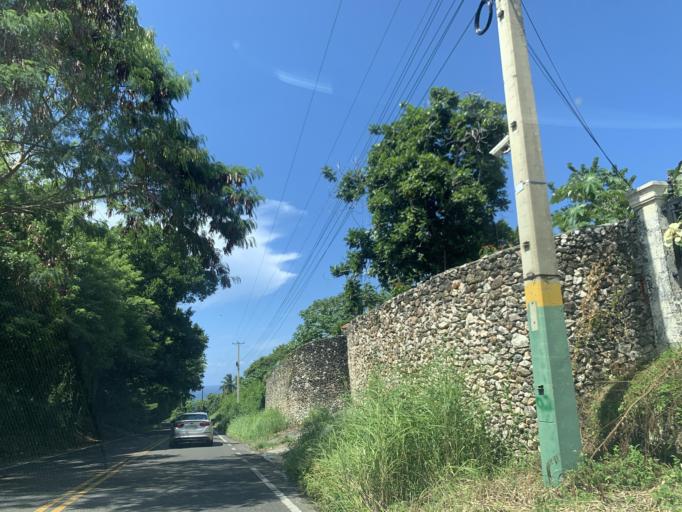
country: DO
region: Maria Trinidad Sanchez
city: Cabrera
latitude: 19.6531
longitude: -69.9337
